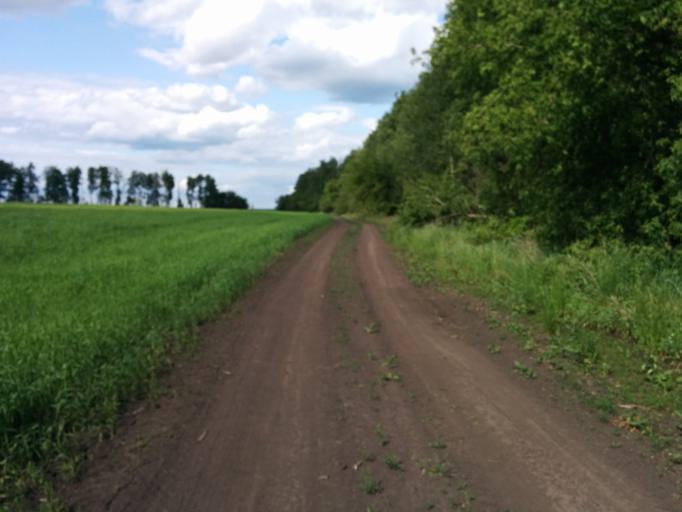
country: RU
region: Tambov
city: Tambov
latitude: 52.8032
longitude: 41.3894
